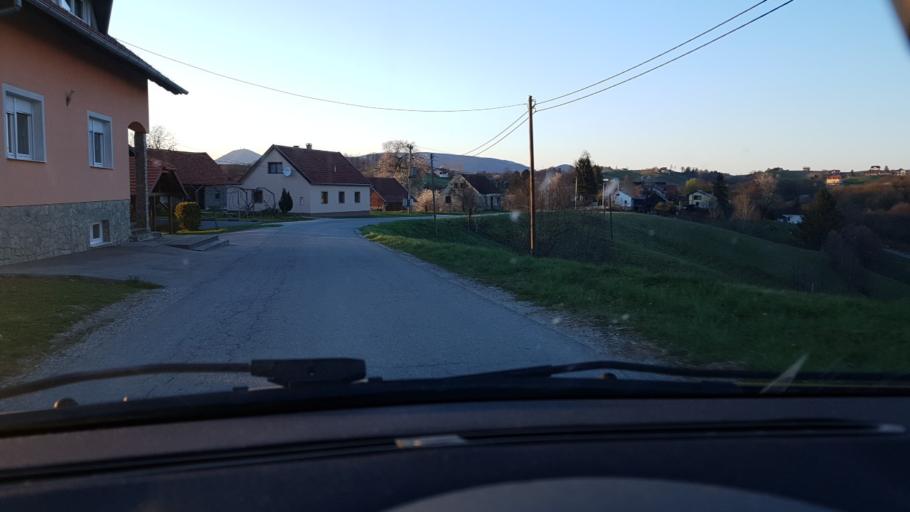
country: SI
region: Rogatec
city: Rogatec
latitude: 46.1906
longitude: 15.6847
